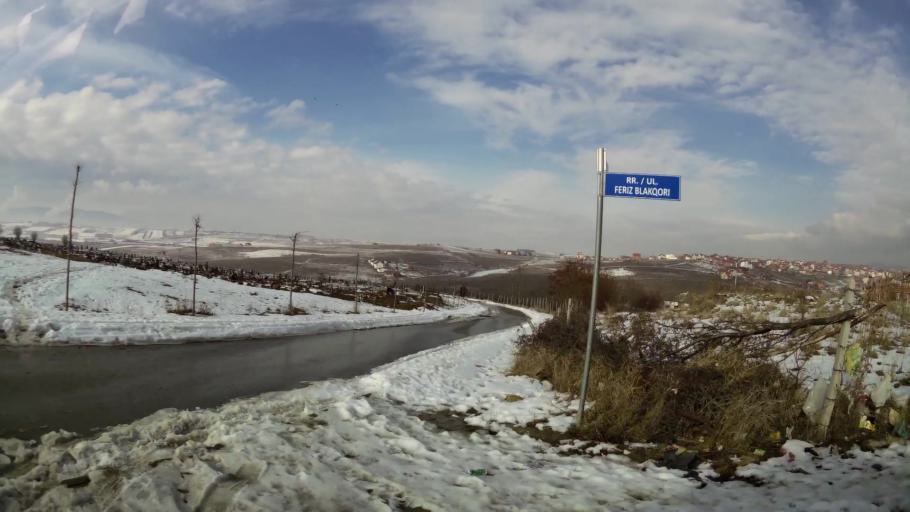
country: XK
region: Pristina
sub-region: Komuna e Prishtines
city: Pristina
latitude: 42.6753
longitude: 21.1514
